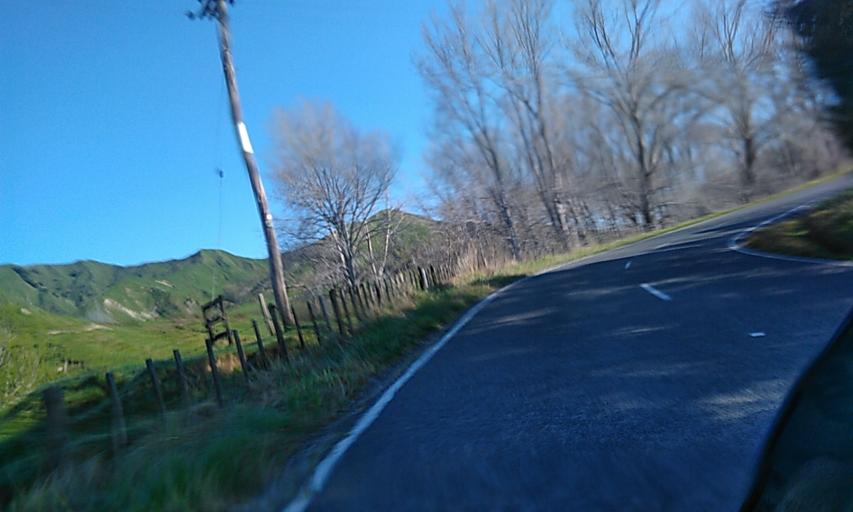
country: NZ
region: Gisborne
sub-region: Gisborne District
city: Gisborne
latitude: -38.5013
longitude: 178.0560
